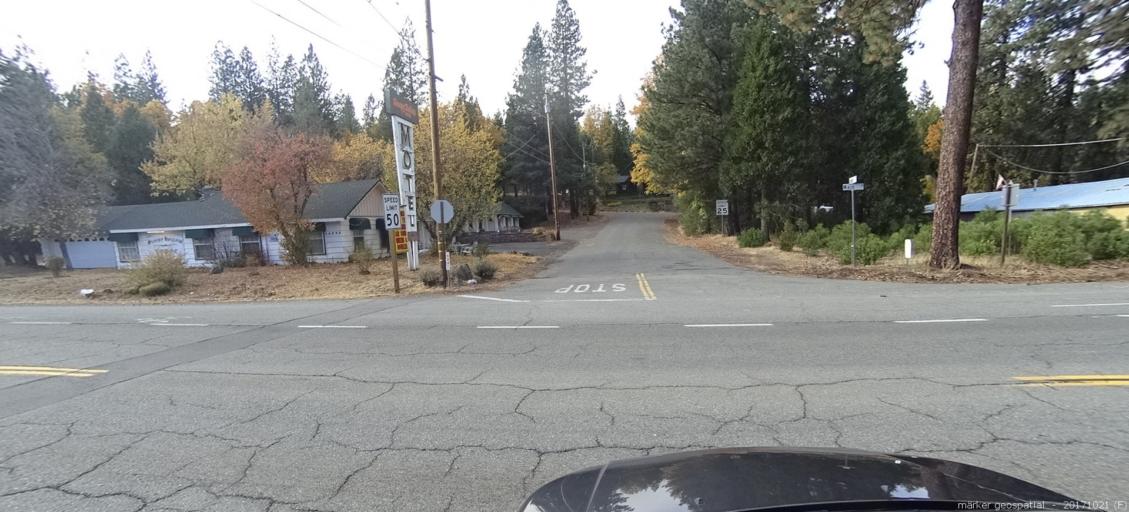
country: US
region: California
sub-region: Shasta County
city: Burney
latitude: 40.8796
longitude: -121.6745
